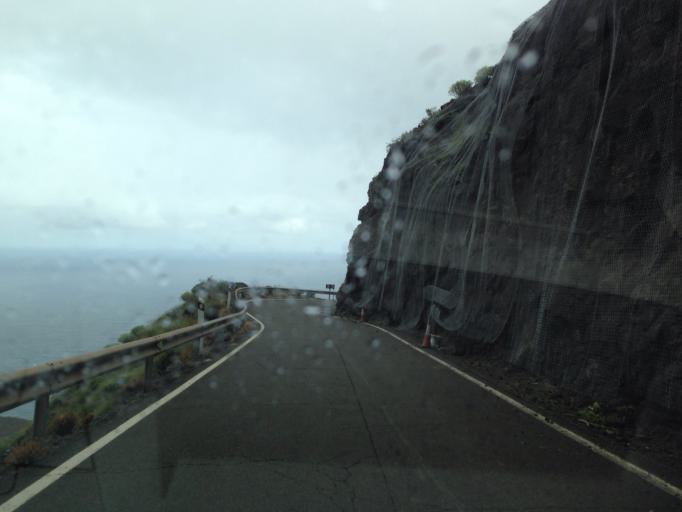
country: ES
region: Canary Islands
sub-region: Provincia de Las Palmas
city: San Nicolas
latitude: 28.0377
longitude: -15.7492
